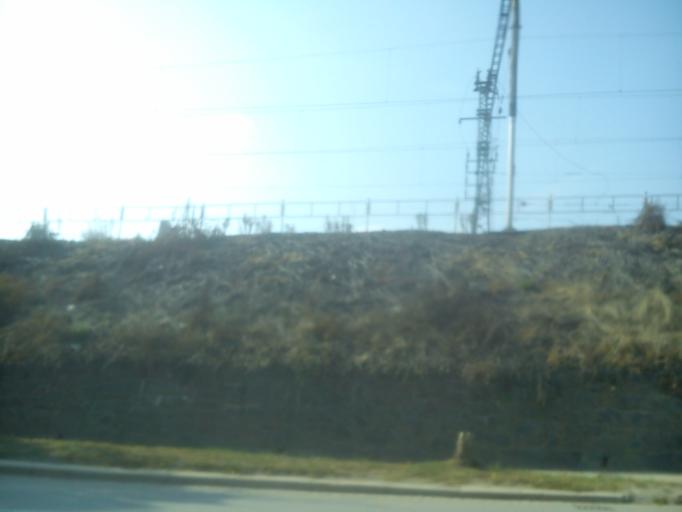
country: CZ
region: South Moravian
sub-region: Mesto Brno
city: Brno
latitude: 49.1850
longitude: 16.6083
